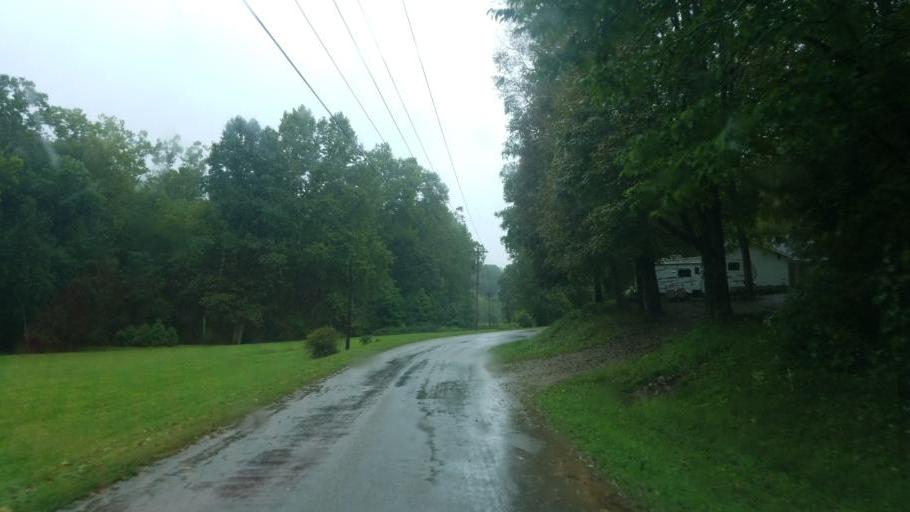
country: US
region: Kentucky
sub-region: Lewis County
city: Vanceburg
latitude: 38.7984
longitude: -83.2548
